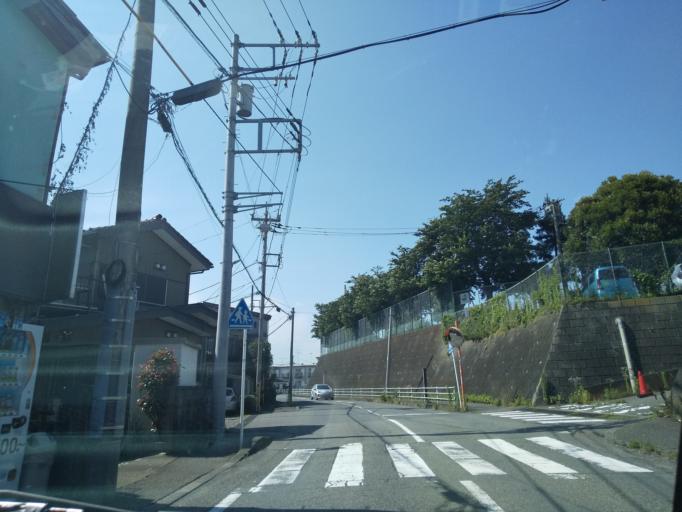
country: JP
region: Kanagawa
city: Minami-rinkan
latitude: 35.4559
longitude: 139.4170
